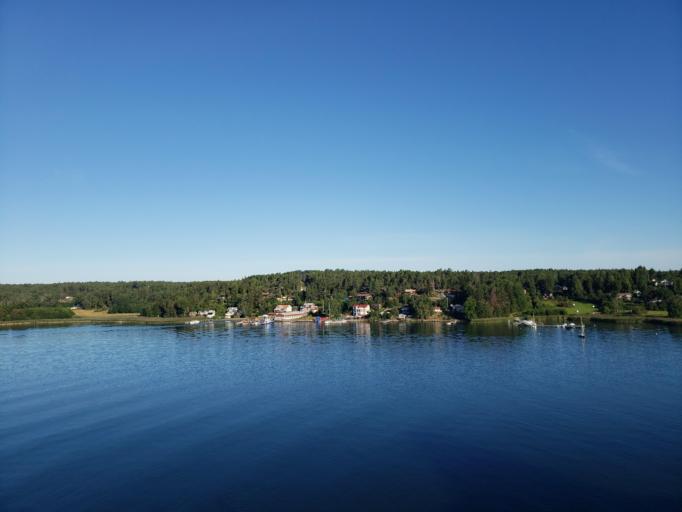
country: SE
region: Stockholm
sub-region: Vaxholms Kommun
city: Vaxholm
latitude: 59.5008
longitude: 18.4698
